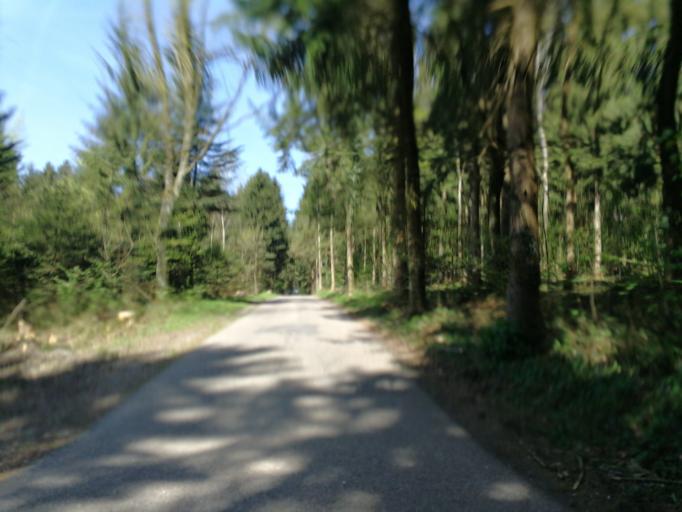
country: CH
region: Zurich
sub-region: Bezirk Hinwil
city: Hinwil
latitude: 47.2952
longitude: 8.8226
